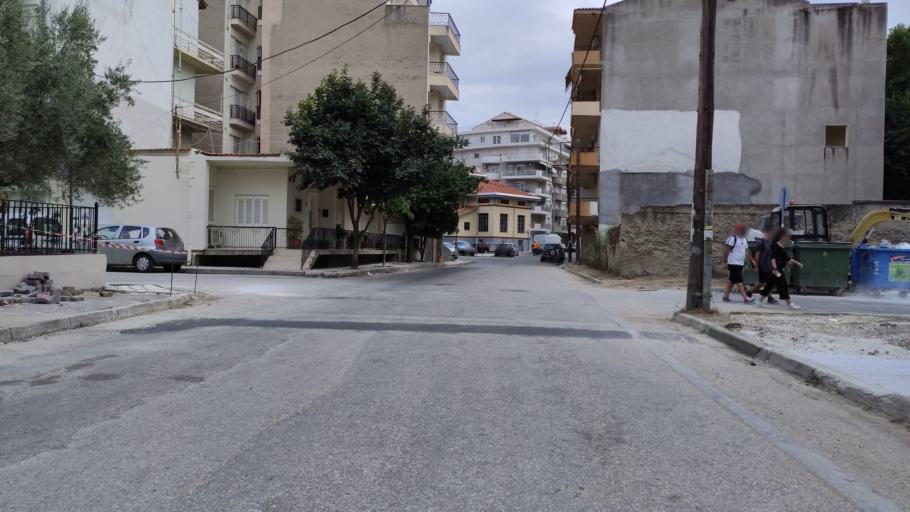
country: GR
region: East Macedonia and Thrace
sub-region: Nomos Rodopis
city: Komotini
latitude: 41.1201
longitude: 25.3951
